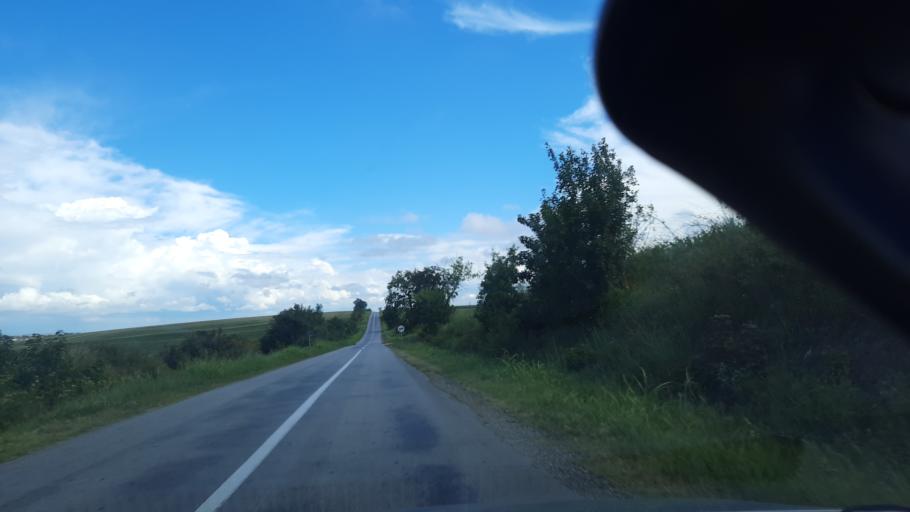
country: RS
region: Autonomna Pokrajina Vojvodina
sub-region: Sremski Okrug
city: Sremska Mitrovica
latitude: 45.0968
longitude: 19.5702
